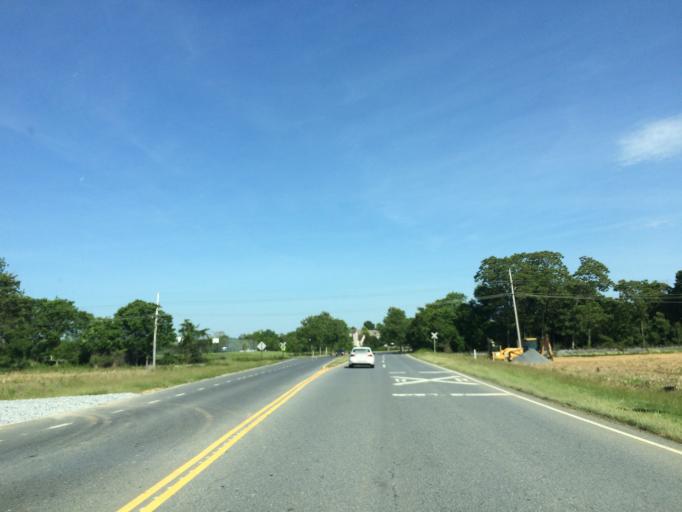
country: US
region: Maryland
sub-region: Frederick County
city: Clover Hill
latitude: 39.4604
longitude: -77.3967
